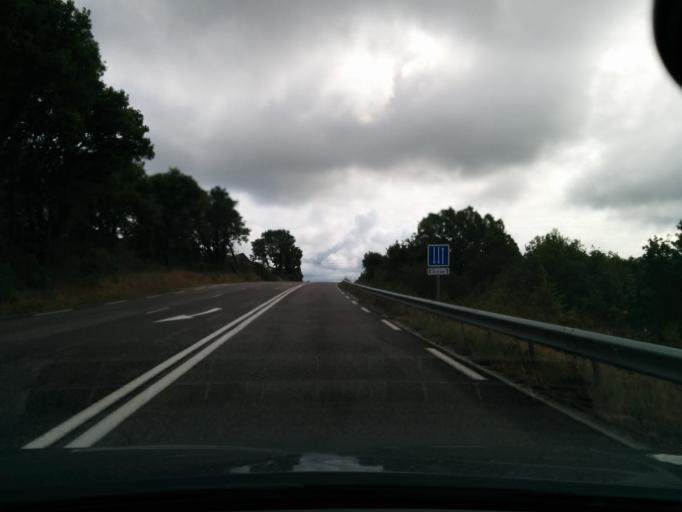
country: FR
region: Midi-Pyrenees
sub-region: Departement du Lot
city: Souillac
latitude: 44.8559
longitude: 1.4657
